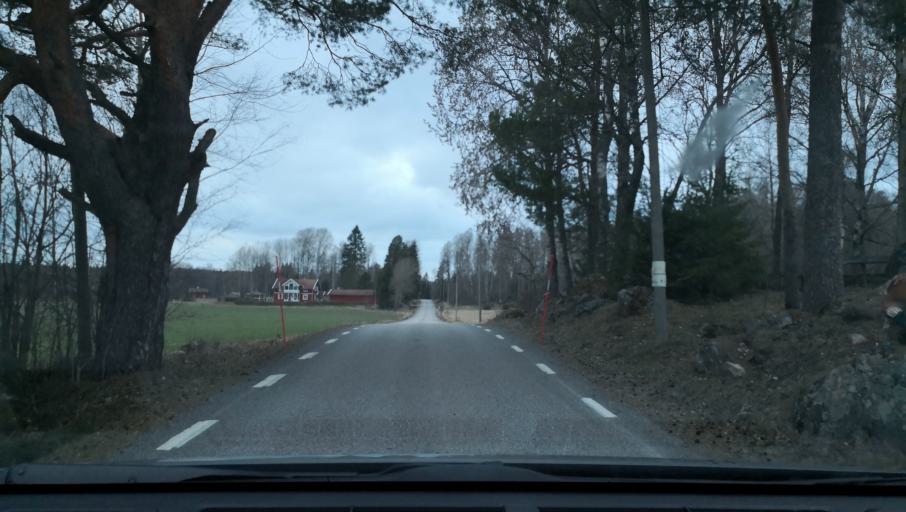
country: SE
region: Vaestmanland
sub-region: Kopings Kommun
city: Kolsva
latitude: 59.5621
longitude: 15.7393
